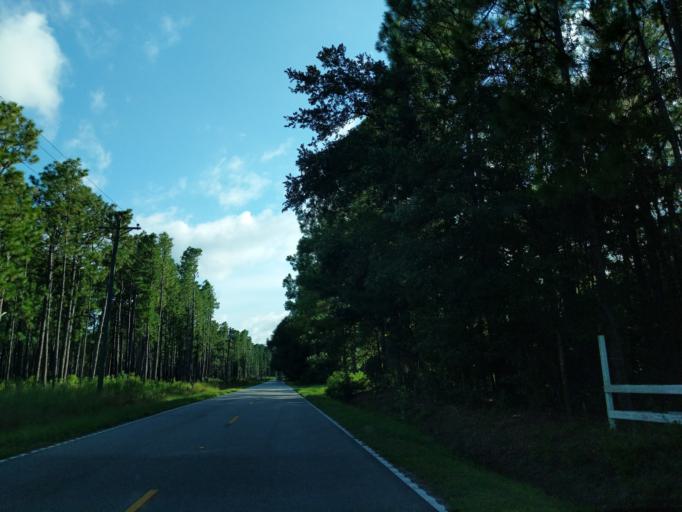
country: US
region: South Carolina
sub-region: Charleston County
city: Awendaw
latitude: 33.1435
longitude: -79.4198
